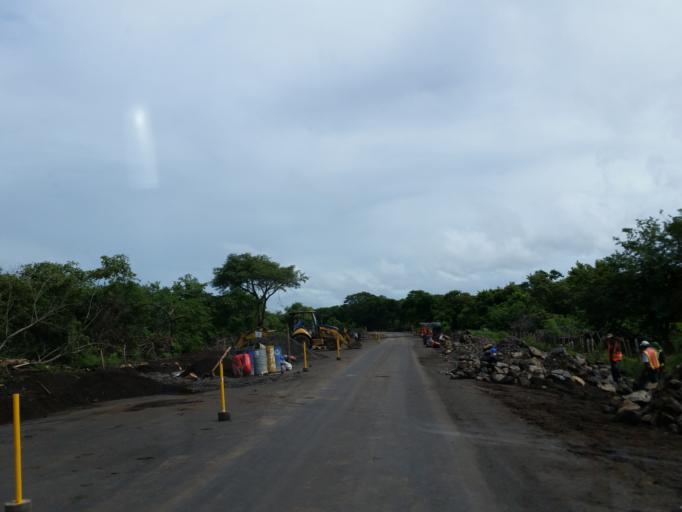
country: NI
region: Leon
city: La Paz Centro
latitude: 12.4596
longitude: -86.6181
